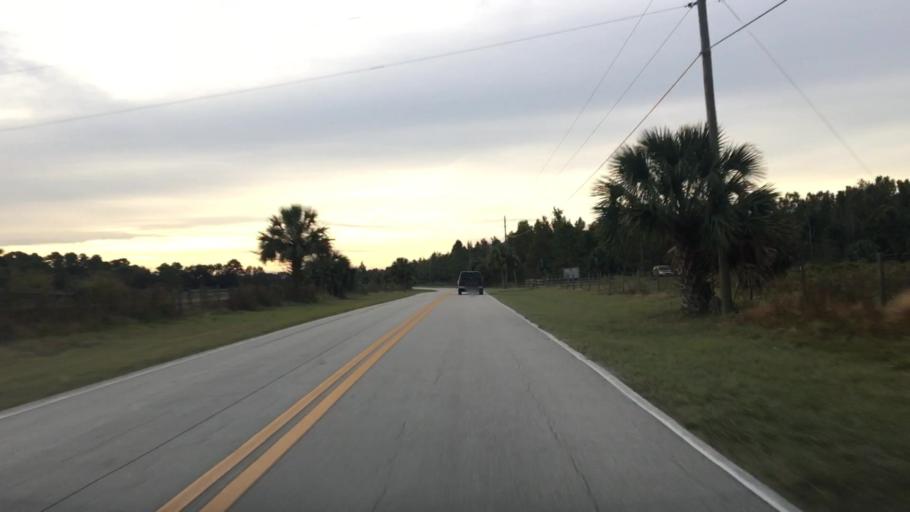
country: US
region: Florida
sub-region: Seminole County
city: Midway
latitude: 28.8327
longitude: -81.1915
